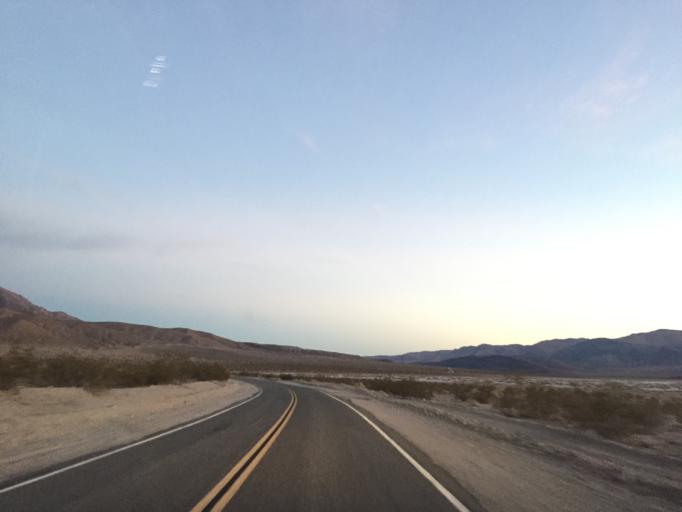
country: US
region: California
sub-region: San Bernardino County
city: Searles Valley
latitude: 35.9829
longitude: -116.7337
